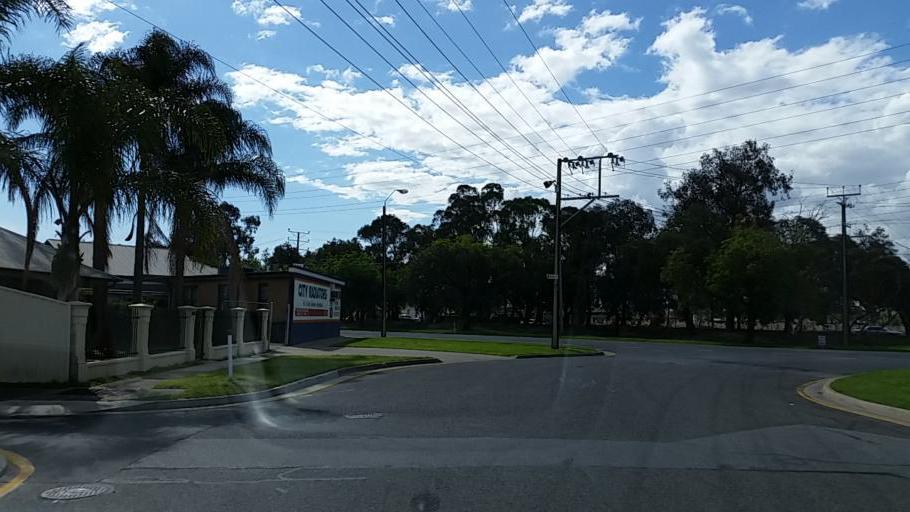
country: AU
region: South Australia
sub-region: Charles Sturt
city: Albert Park
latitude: -34.8738
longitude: 138.5236
